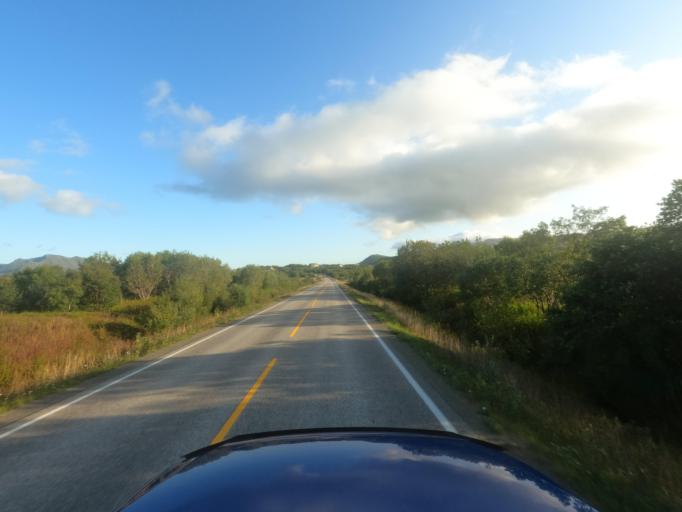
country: NO
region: Nordland
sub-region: Vestvagoy
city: Gravdal
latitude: 68.1471
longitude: 13.5460
